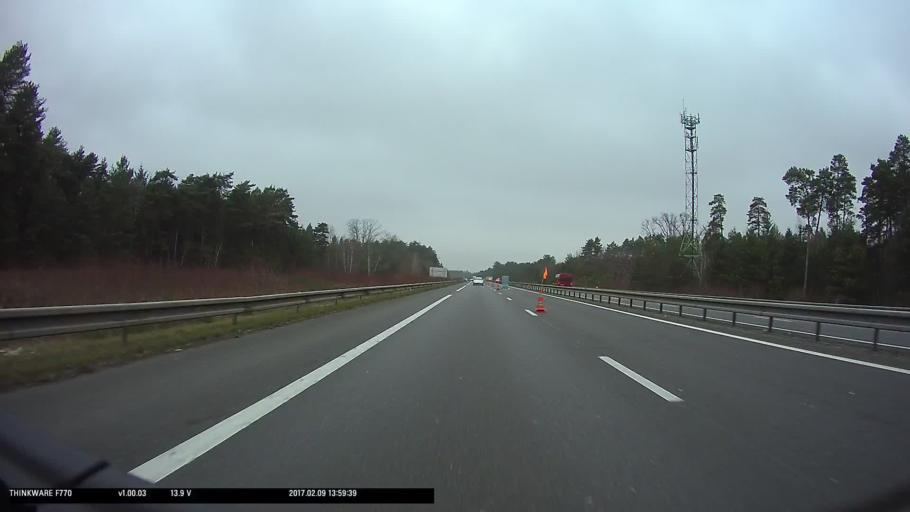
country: FR
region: Centre
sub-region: Departement du Loir-et-Cher
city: Lamotte-Beuvron
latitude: 47.5874
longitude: 1.9905
